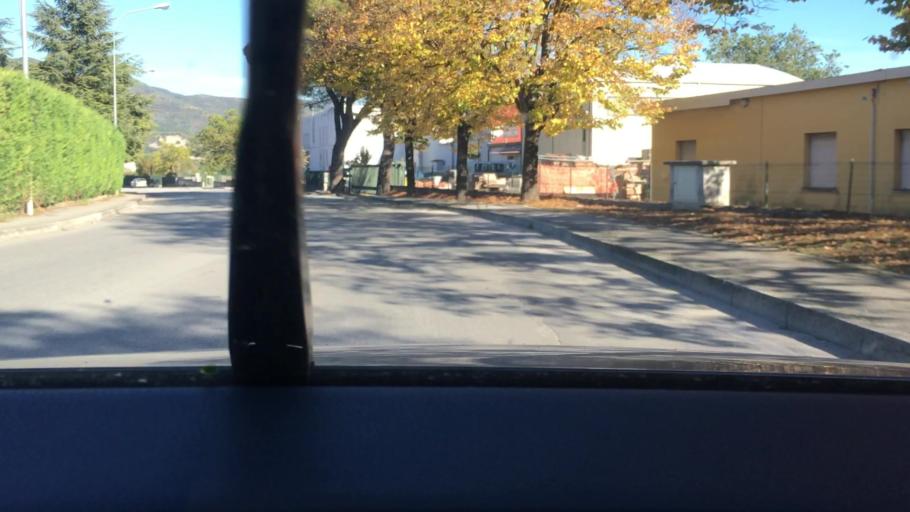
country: IT
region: The Marches
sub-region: Provincia di Ancona
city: Fabriano
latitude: 43.3491
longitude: 12.9131
